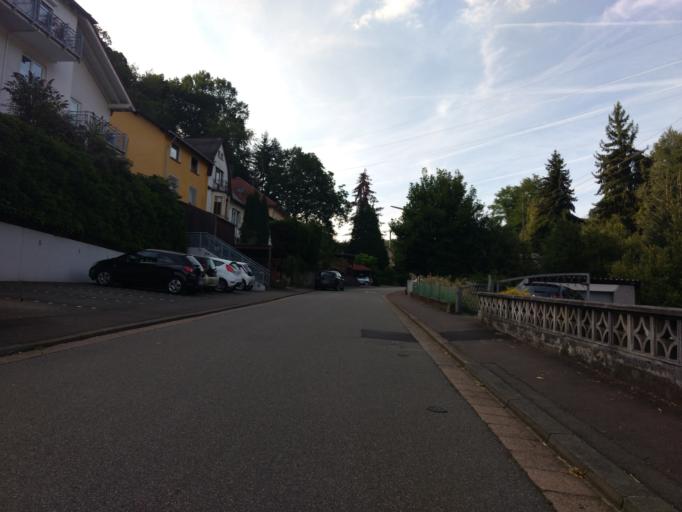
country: DE
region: Saarland
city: Beckingen
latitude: 49.3978
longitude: 6.7004
